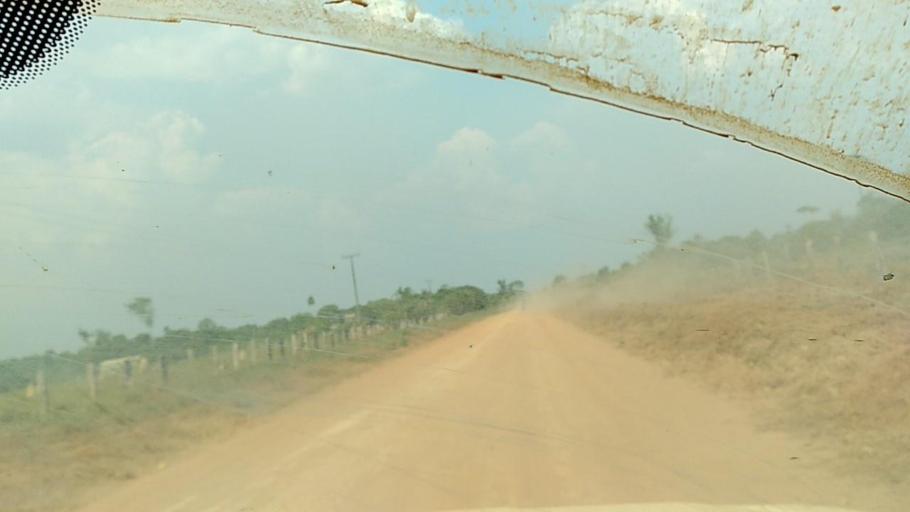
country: BR
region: Rondonia
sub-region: Porto Velho
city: Porto Velho
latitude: -8.6832
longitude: -63.2110
